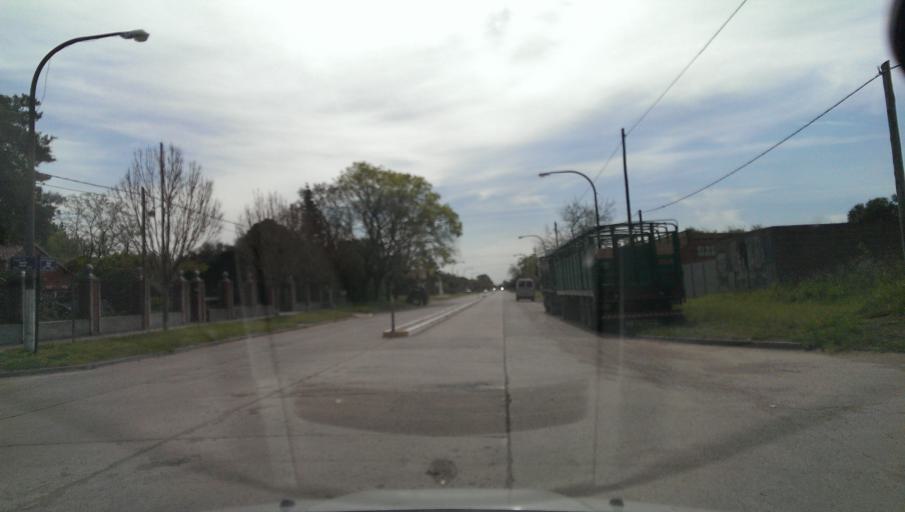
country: AR
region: Buenos Aires
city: Tapalque
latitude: -36.3860
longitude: -59.4947
